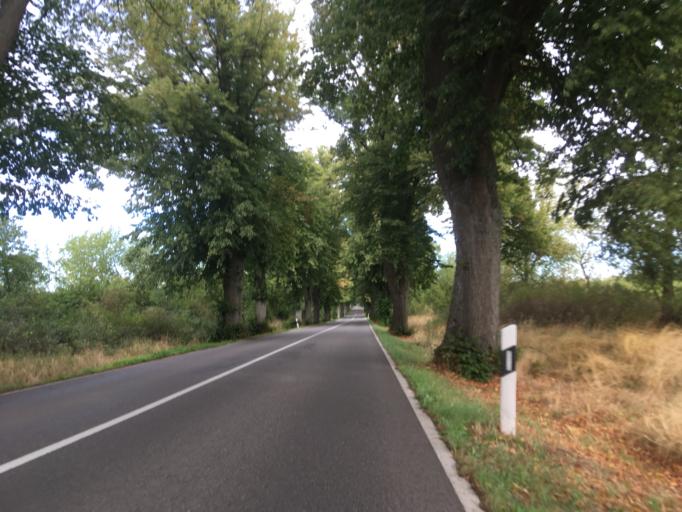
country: DE
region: Brandenburg
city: Templin
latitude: 53.1971
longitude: 13.5615
